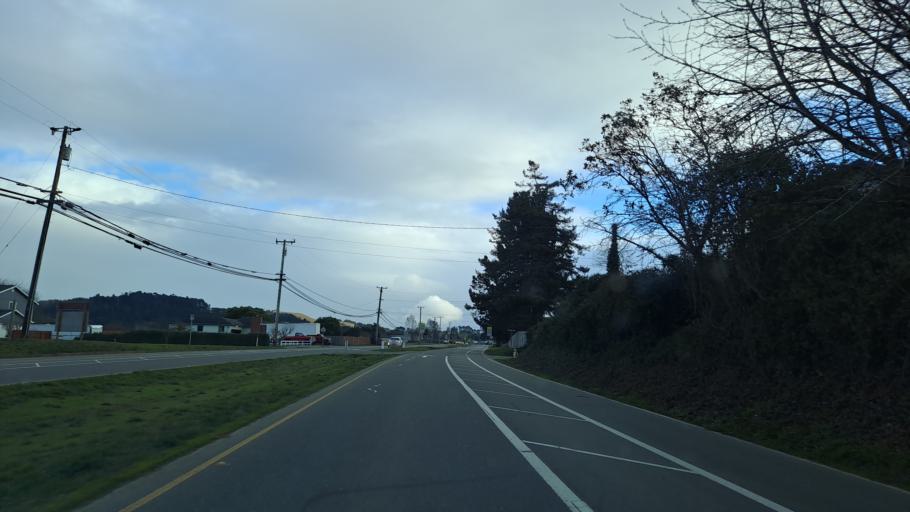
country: US
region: California
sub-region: Humboldt County
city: Fortuna
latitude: 40.5749
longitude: -124.1442
